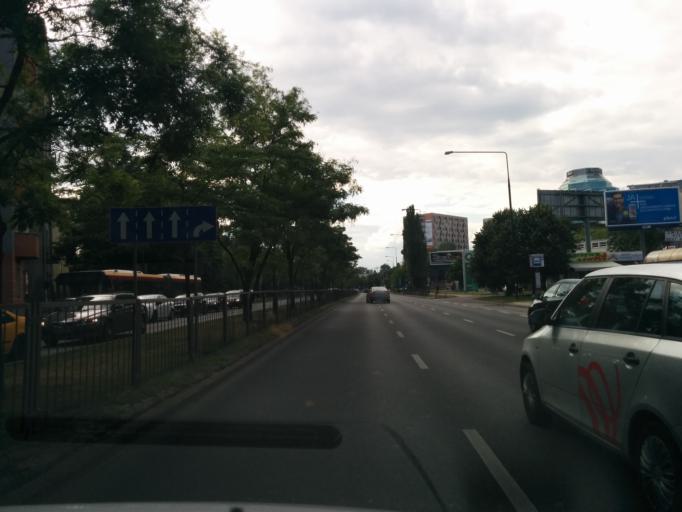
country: PL
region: Masovian Voivodeship
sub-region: Warszawa
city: Ochota
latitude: 52.2179
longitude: 20.9770
